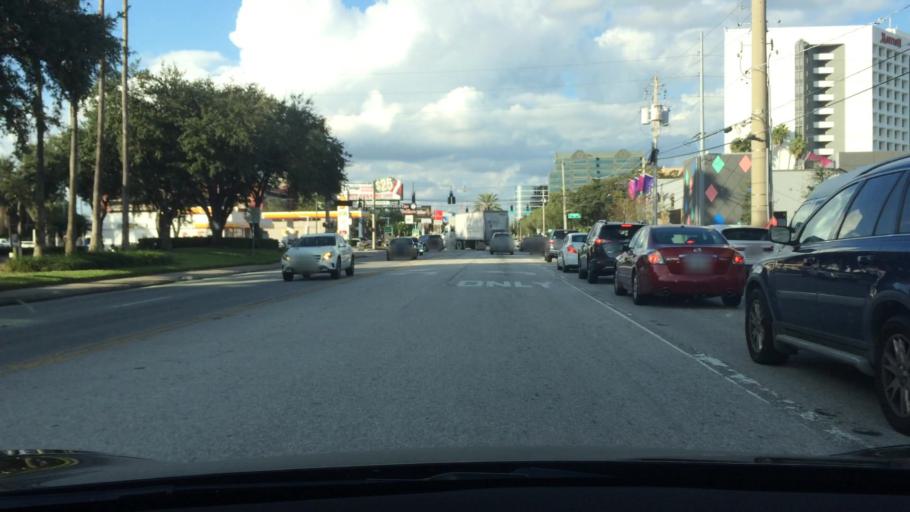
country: US
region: Florida
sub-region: Hillsborough County
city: Tampa
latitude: 27.9514
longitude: -82.5241
